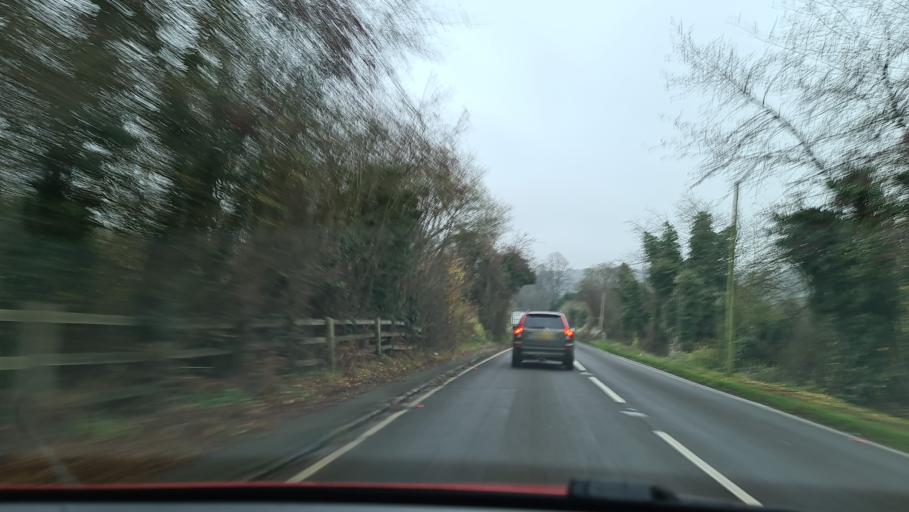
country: GB
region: England
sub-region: Buckinghamshire
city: Stokenchurch
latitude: 51.6427
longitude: -0.8373
